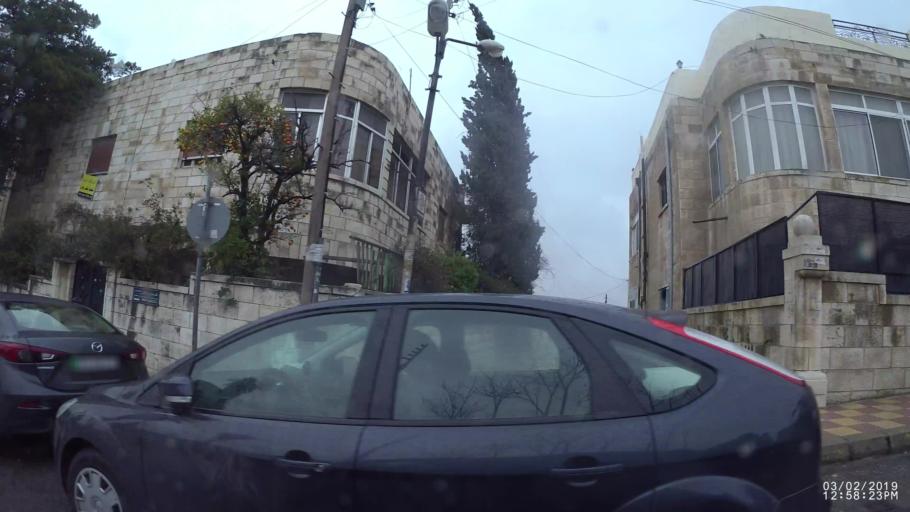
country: JO
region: Amman
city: Amman
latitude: 31.9547
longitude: 35.9294
